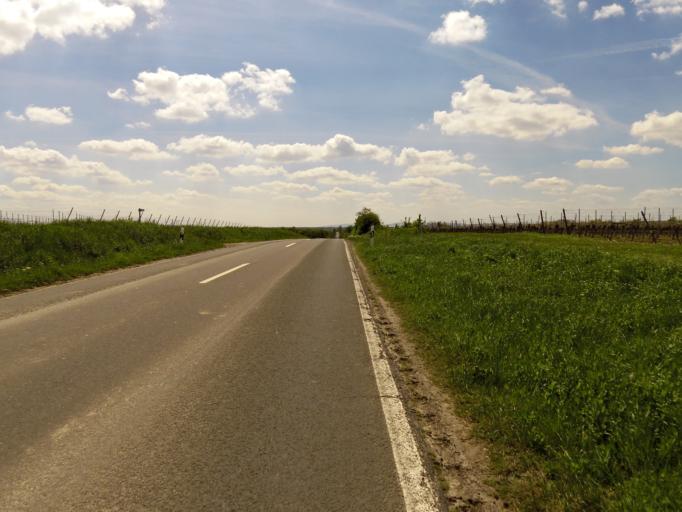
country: DE
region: Rheinland-Pfalz
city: Westhofen
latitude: 49.6919
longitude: 8.2410
